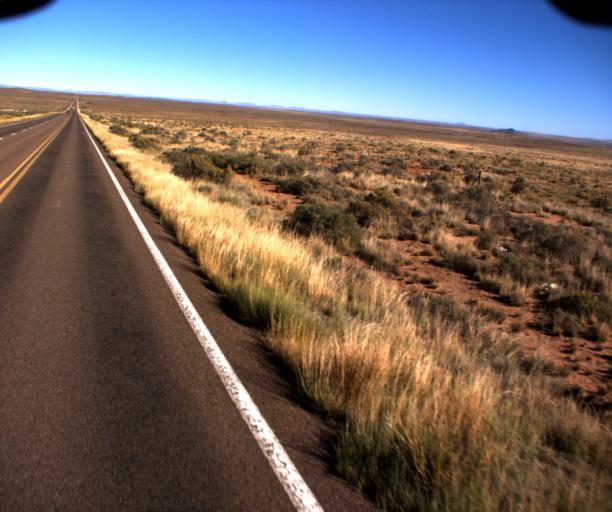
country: US
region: Arizona
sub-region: Navajo County
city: Snowflake
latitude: 34.6932
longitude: -110.1067
